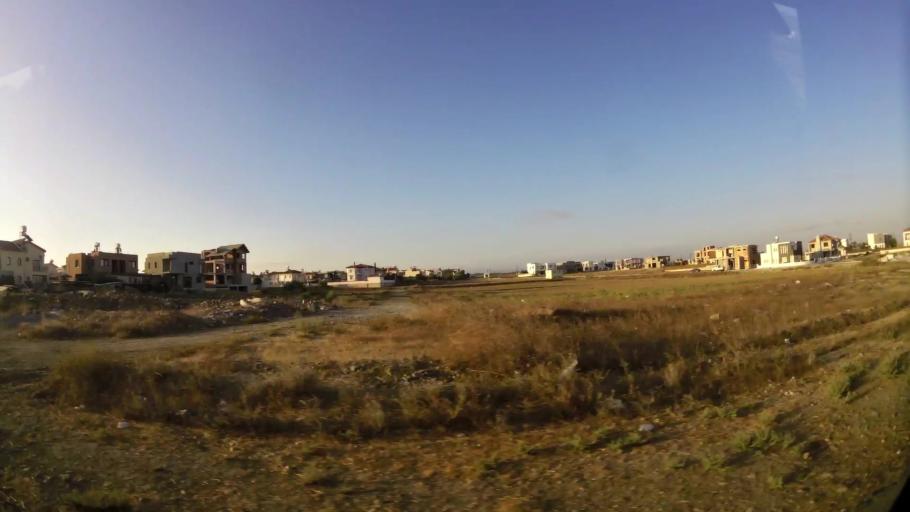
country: CY
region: Lefkosia
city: Nicosia
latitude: 35.1956
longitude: 33.3159
